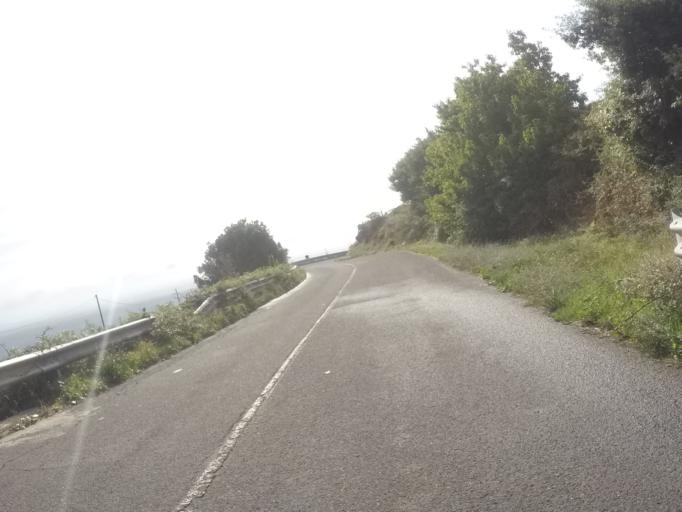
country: IT
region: Sardinia
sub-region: Provincia di Oristano
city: Santu Lussurgiu
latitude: 40.1633
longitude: 8.6599
